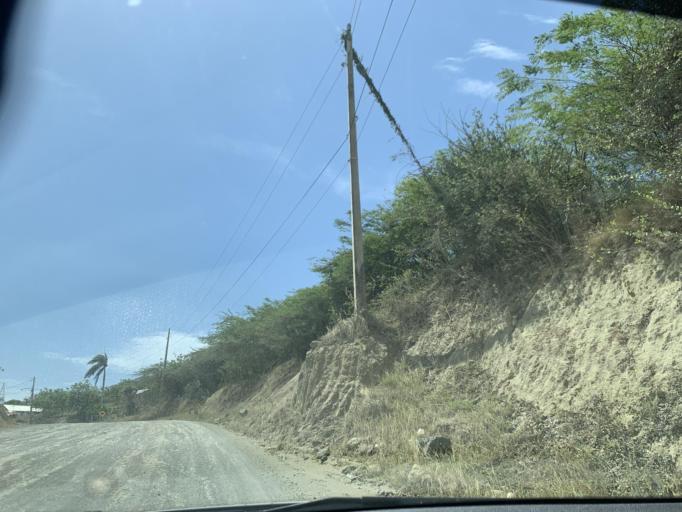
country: DO
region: Puerto Plata
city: Imbert
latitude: 19.8664
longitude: -70.8130
